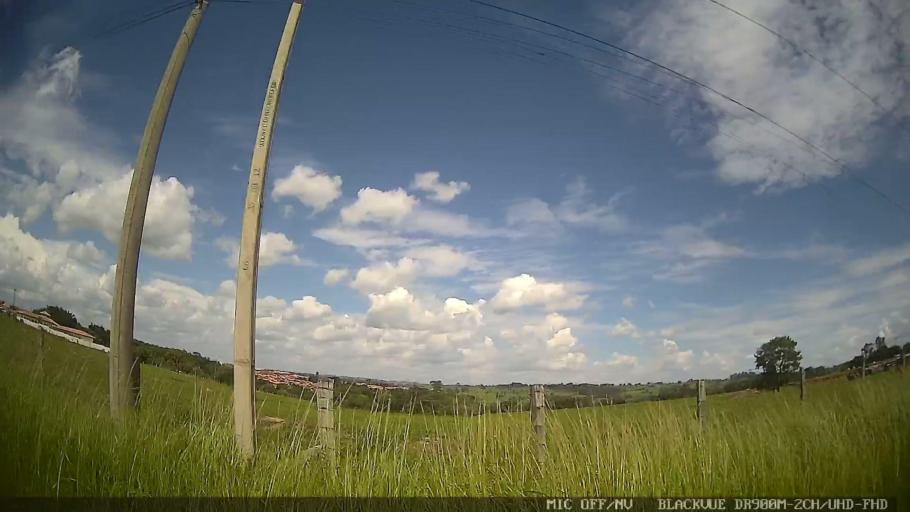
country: BR
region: Sao Paulo
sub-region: Conchas
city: Conchas
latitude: -23.0420
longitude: -48.0224
